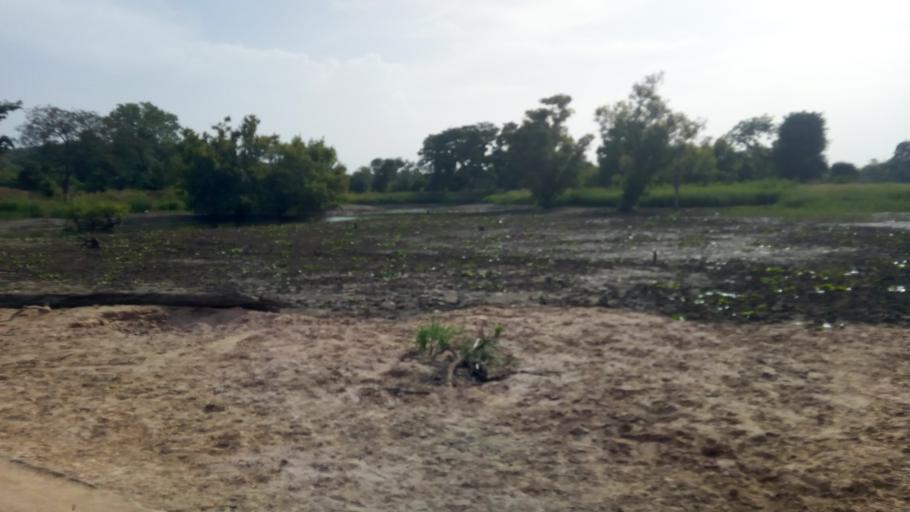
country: ML
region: Kayes
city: Kita
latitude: 13.1420
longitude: -8.8750
